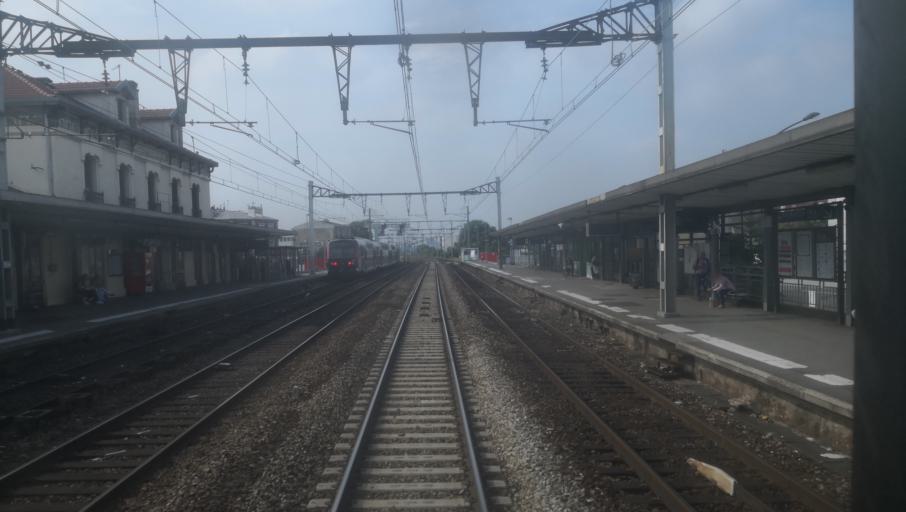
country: FR
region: Ile-de-France
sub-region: Departement du Val-de-Marne
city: Vitry-sur-Seine
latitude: 48.8001
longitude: 2.4027
